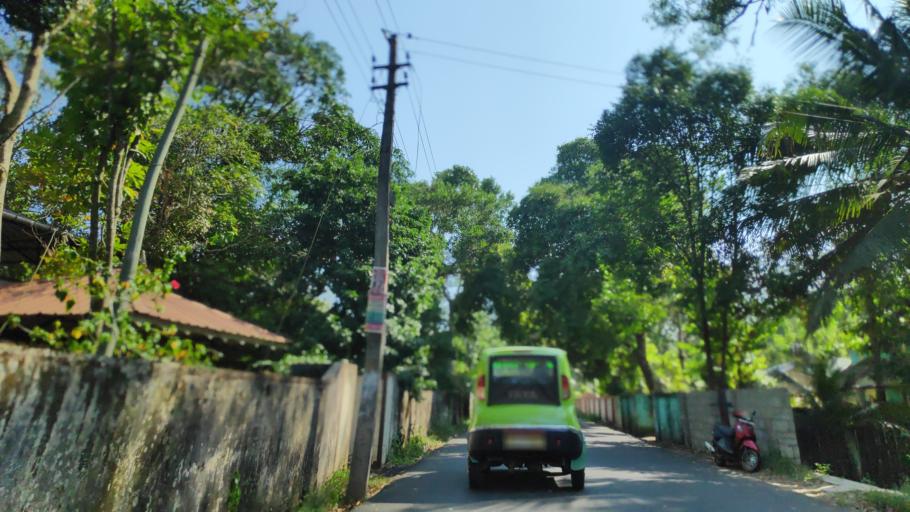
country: IN
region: Kerala
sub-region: Alappuzha
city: Alleppey
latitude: 9.5735
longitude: 76.3167
